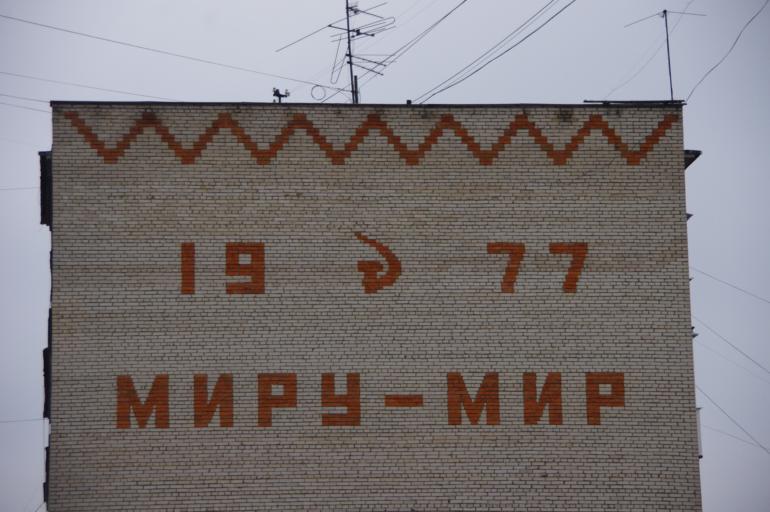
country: RU
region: Moskovskaya
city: Opalikha
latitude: 55.8409
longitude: 37.2574
